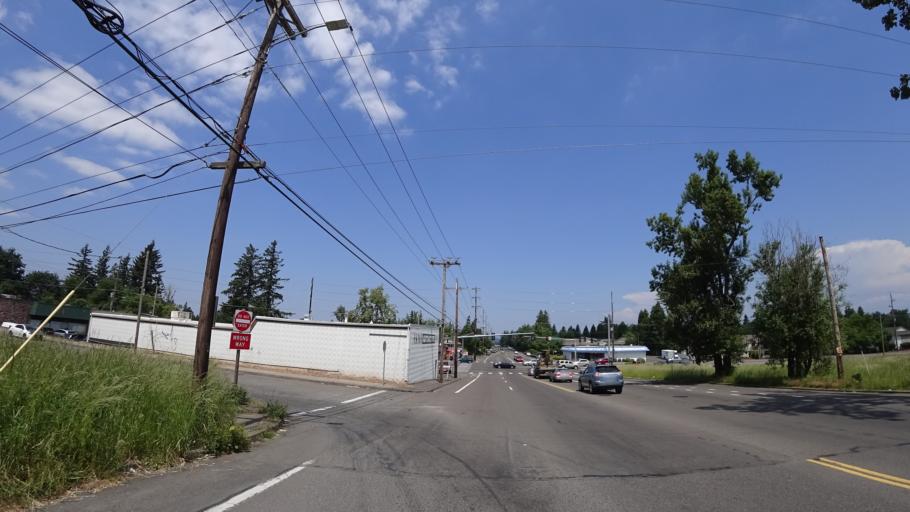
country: US
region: Oregon
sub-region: Multnomah County
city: Fairview
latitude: 45.5334
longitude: -122.4960
